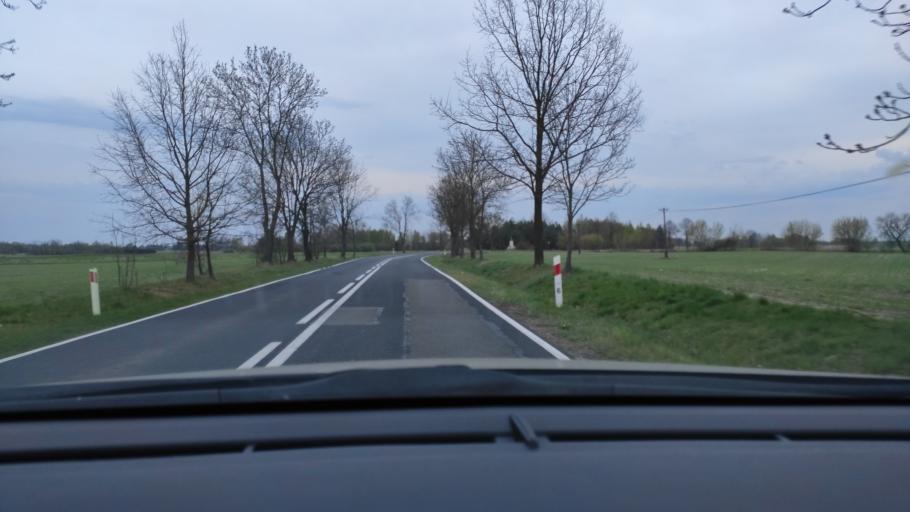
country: PL
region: Masovian Voivodeship
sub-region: Powiat zwolenski
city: Zwolen
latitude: 51.3810
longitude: 21.5609
